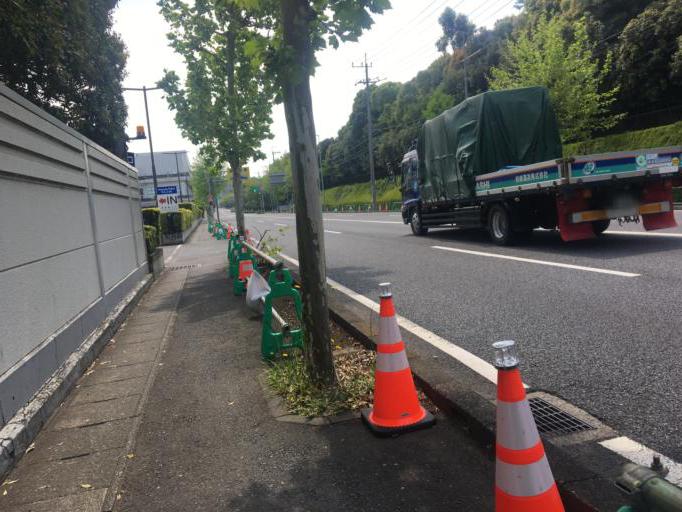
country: JP
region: Saitama
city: Wako
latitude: 35.7818
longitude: 139.6132
